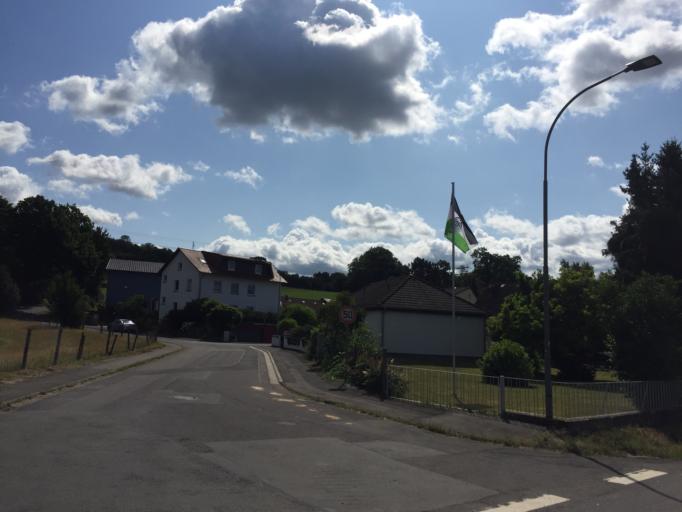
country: DE
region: Hesse
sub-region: Regierungsbezirk Giessen
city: Grunberg
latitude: 50.5833
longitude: 8.9660
